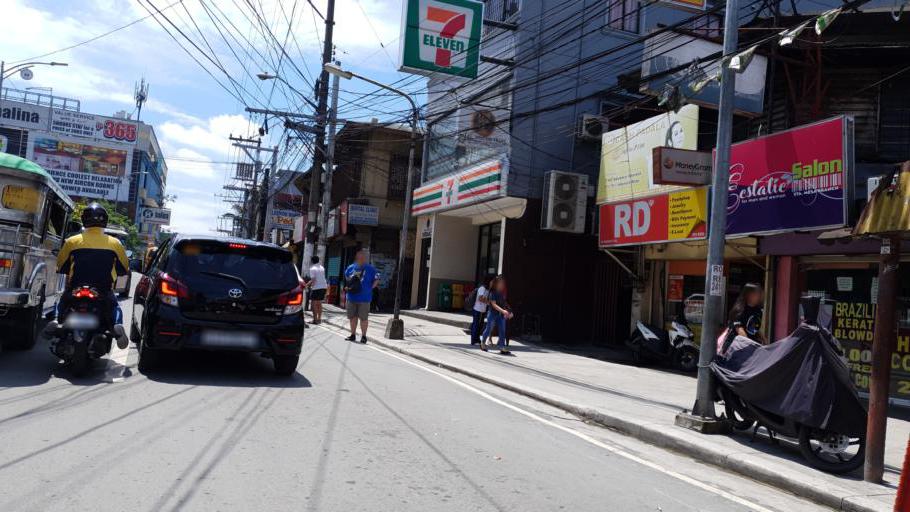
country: PH
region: Metro Manila
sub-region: San Juan
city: San Juan
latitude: 14.6007
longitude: 121.0133
